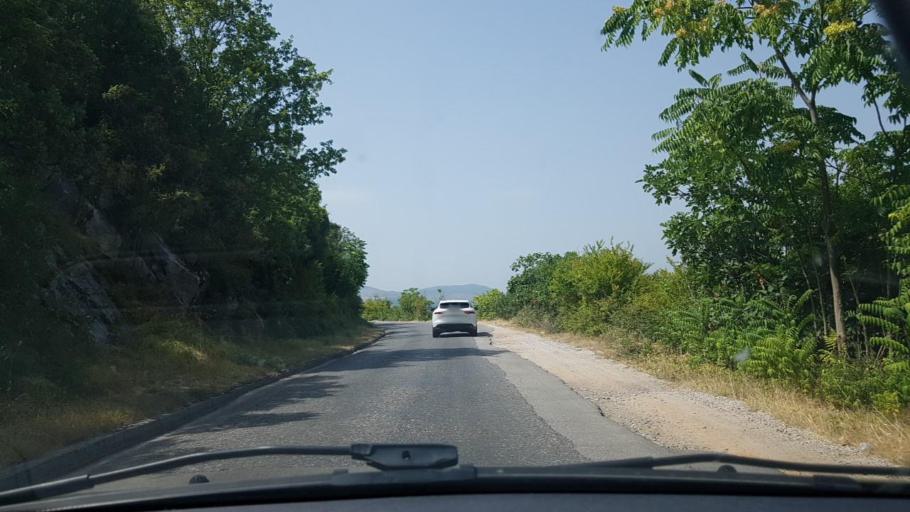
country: BA
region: Federation of Bosnia and Herzegovina
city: Tasovcici
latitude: 43.0287
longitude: 17.7455
